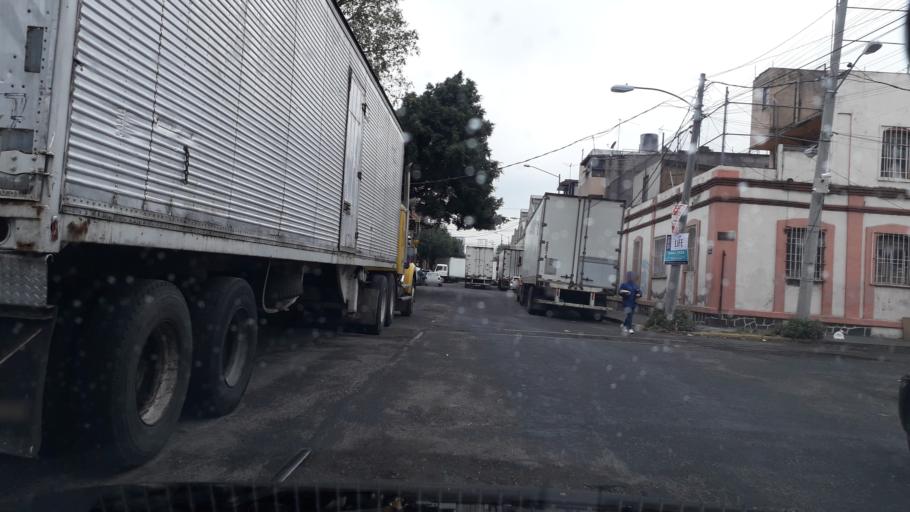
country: MX
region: Mexico City
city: Cuauhtemoc
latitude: 19.4586
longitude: -99.1605
